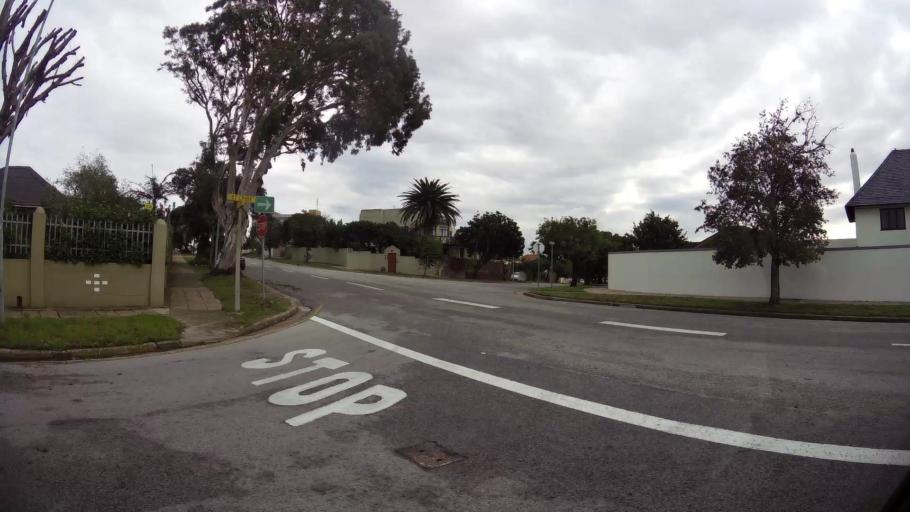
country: ZA
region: Eastern Cape
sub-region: Nelson Mandela Bay Metropolitan Municipality
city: Port Elizabeth
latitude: -33.9562
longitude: 25.5985
